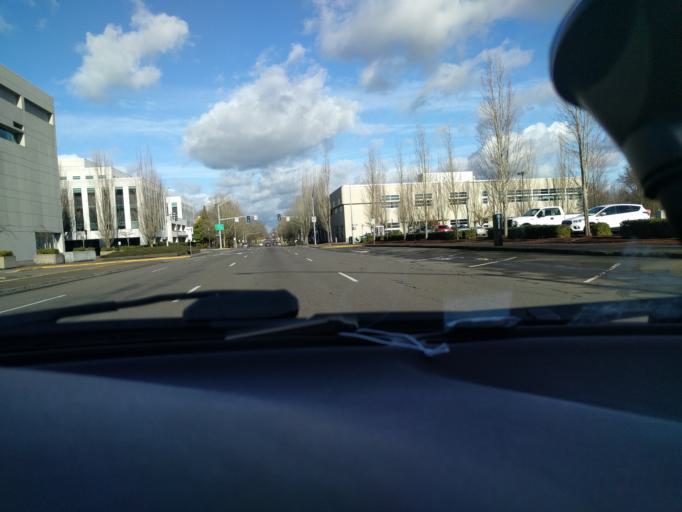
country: US
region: Oregon
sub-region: Marion County
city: Salem
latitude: 44.9411
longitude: -123.0273
